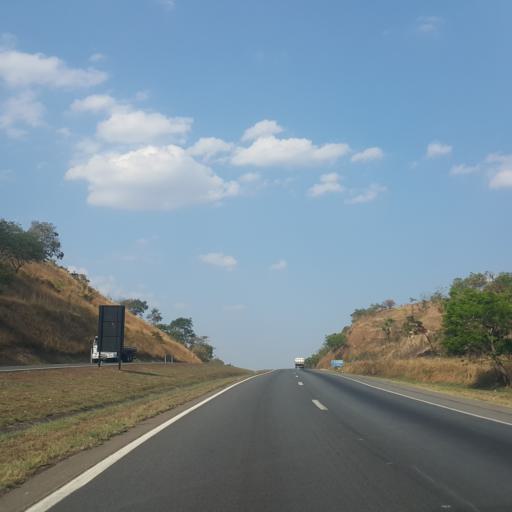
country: BR
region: Goias
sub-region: Abadiania
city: Abadiania
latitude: -16.1095
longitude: -48.5816
